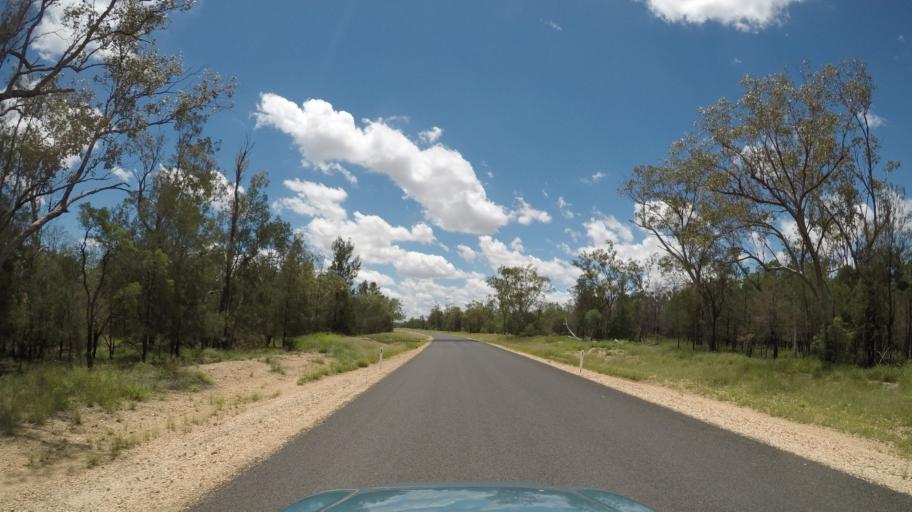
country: AU
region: Queensland
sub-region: Goondiwindi
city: Goondiwindi
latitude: -28.1553
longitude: 150.1222
